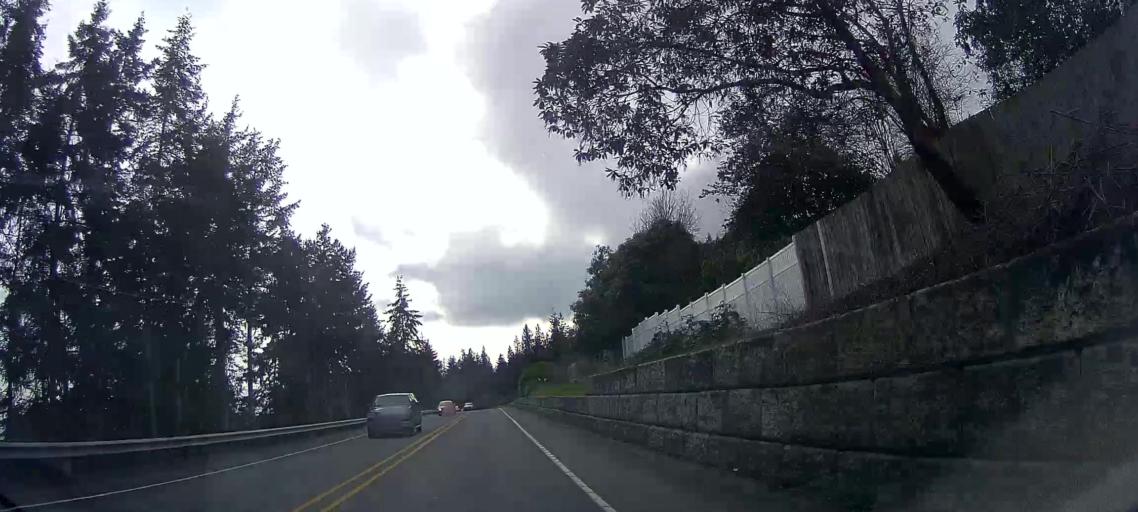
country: US
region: Washington
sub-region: Island County
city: Camano
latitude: 48.1861
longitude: -122.4806
